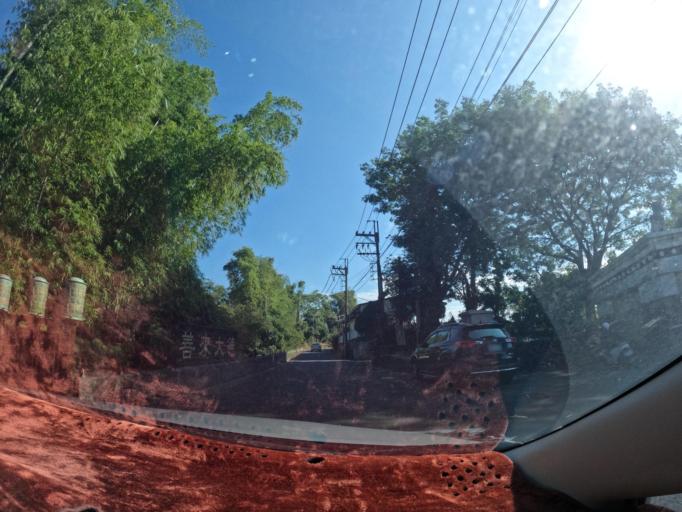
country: TW
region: Taiwan
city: Yujing
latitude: 23.0539
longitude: 120.4002
